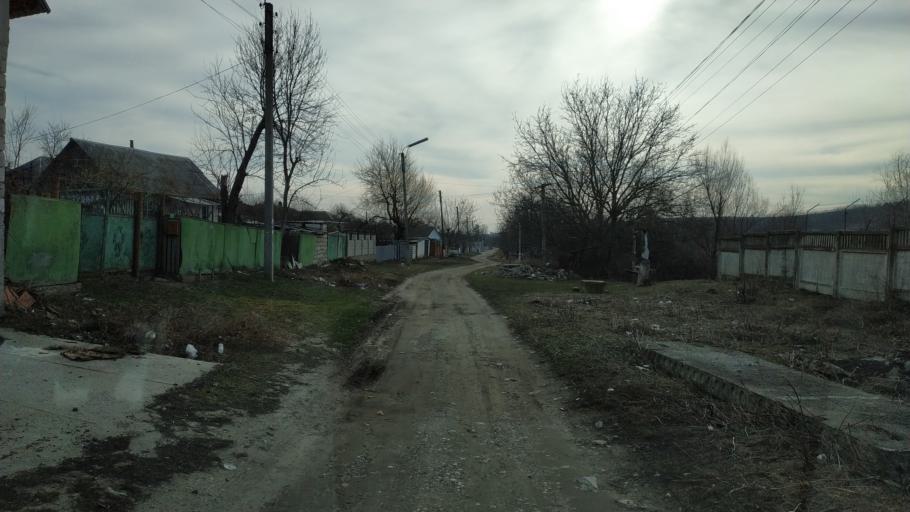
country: MD
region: Chisinau
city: Vatra
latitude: 46.9825
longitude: 28.6713
